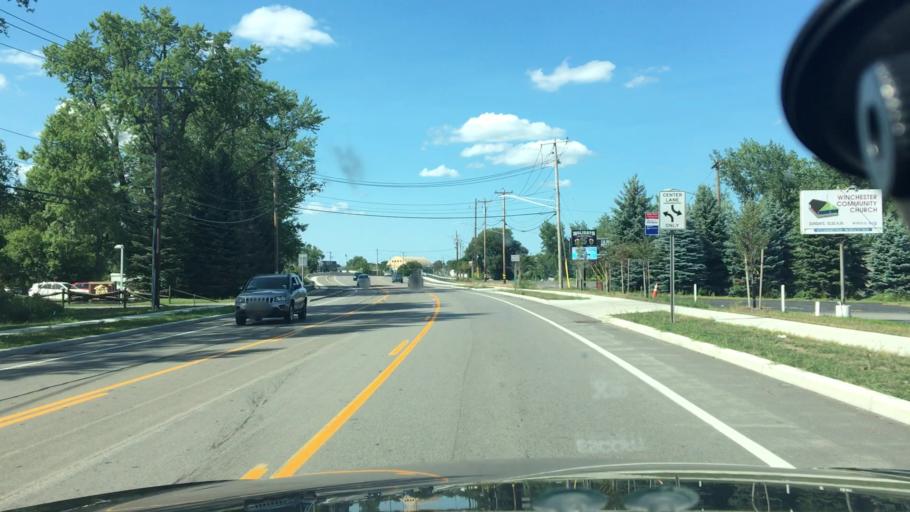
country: US
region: New York
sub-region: Erie County
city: West Seneca
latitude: 42.8678
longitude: -78.7871
